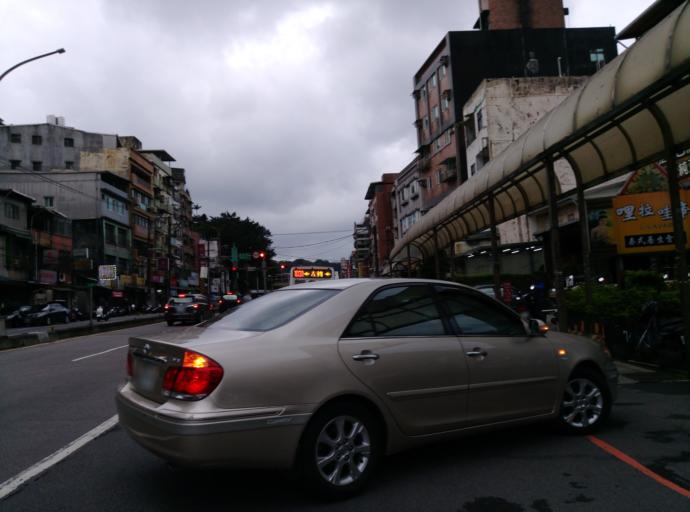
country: TW
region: Taiwan
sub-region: Keelung
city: Keelung
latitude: 25.1239
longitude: 121.7428
